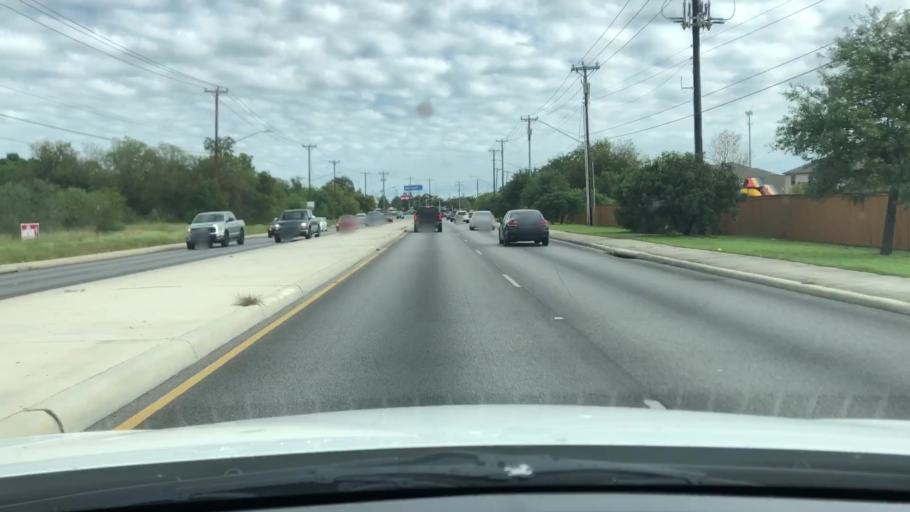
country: US
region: Texas
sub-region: Bexar County
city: Leon Valley
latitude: 29.4879
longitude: -98.6734
